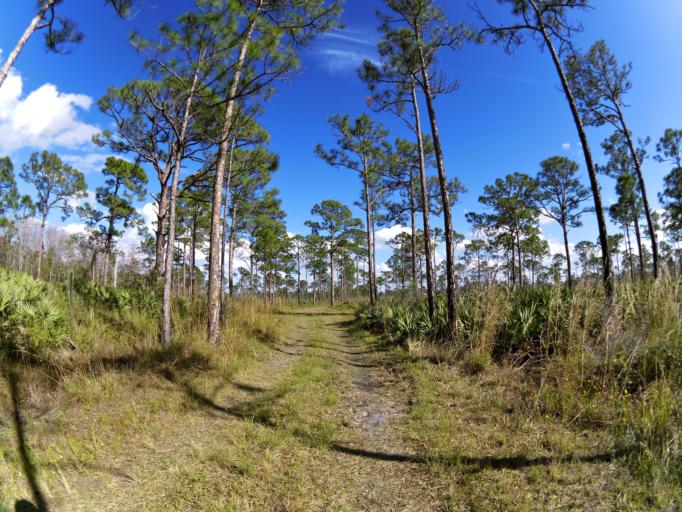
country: US
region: Florida
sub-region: Martin County
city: Hobe Sound
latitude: 27.0205
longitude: -80.1545
